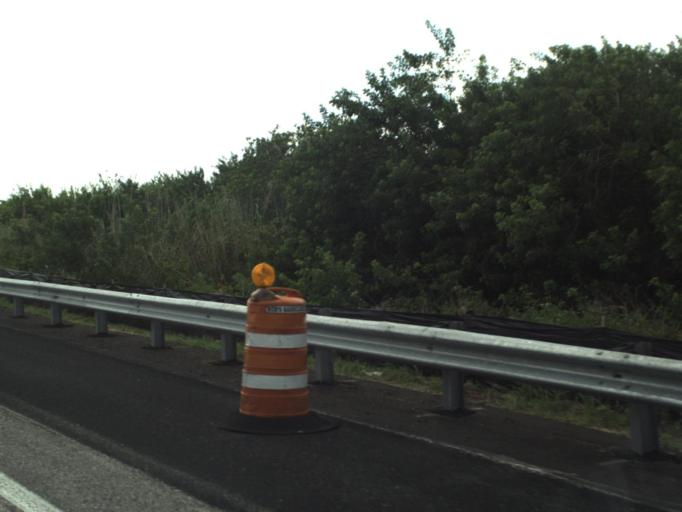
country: US
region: Florida
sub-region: Palm Beach County
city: Loxahatchee Groves
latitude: 26.7254
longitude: -80.4496
